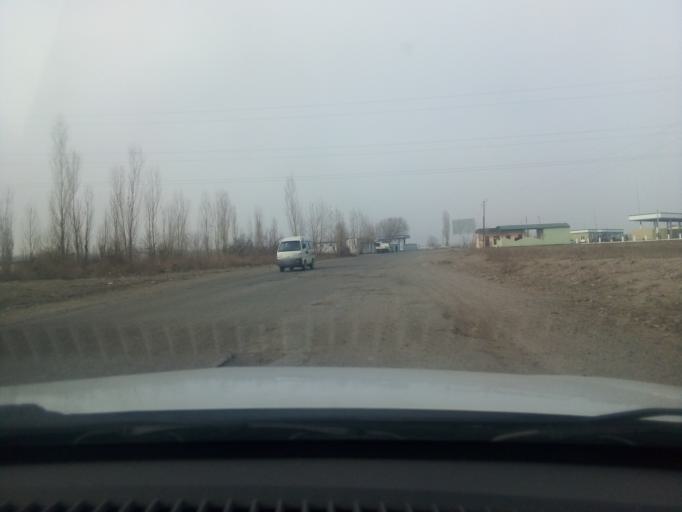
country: UZ
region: Namangan
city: Pop Shahri
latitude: 40.9077
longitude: 71.1024
